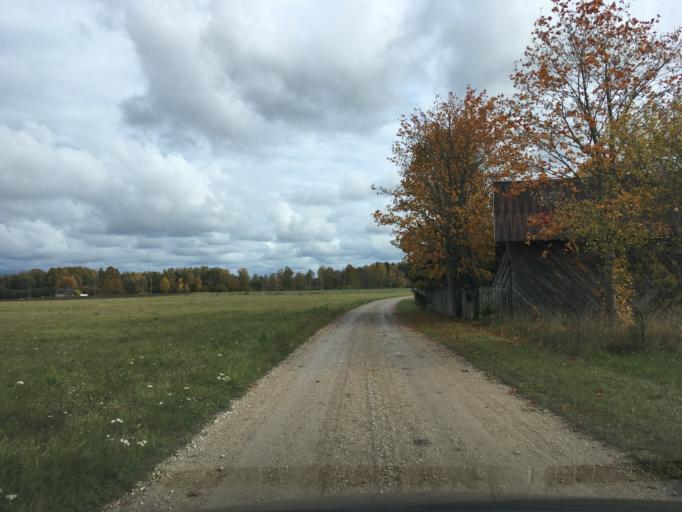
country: EE
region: Harju
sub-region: Raasiku vald
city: Raasiku
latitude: 59.2154
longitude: 25.2137
